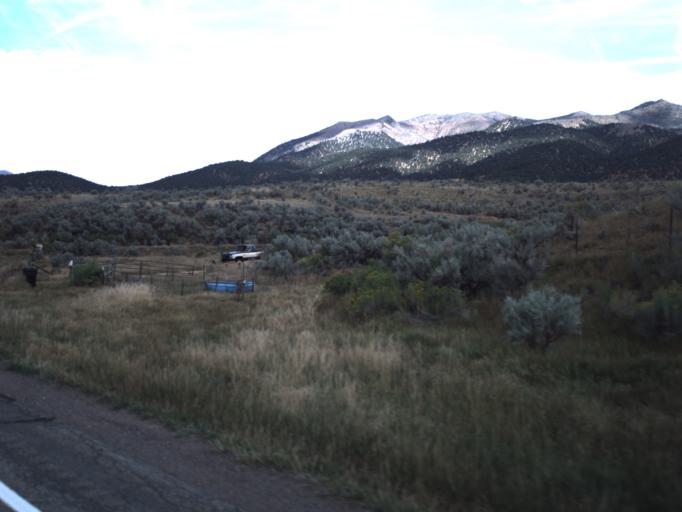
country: US
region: Utah
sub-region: Utah County
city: Woodland Hills
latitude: 39.8610
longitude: -111.5274
